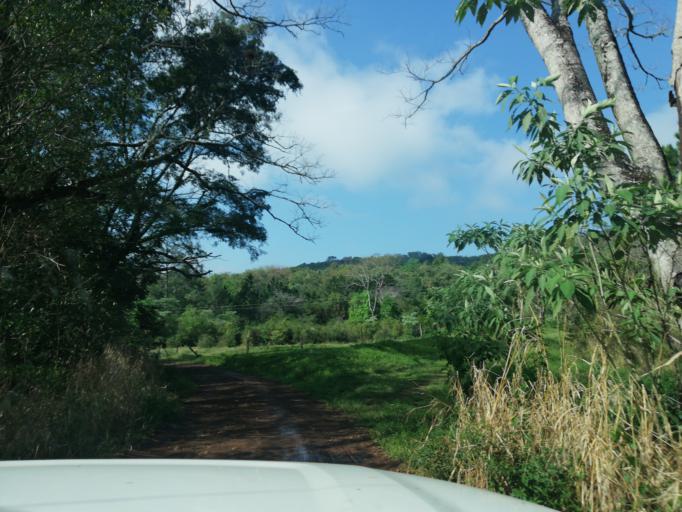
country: AR
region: Misiones
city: Cerro Azul
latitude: -27.6123
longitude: -55.5302
